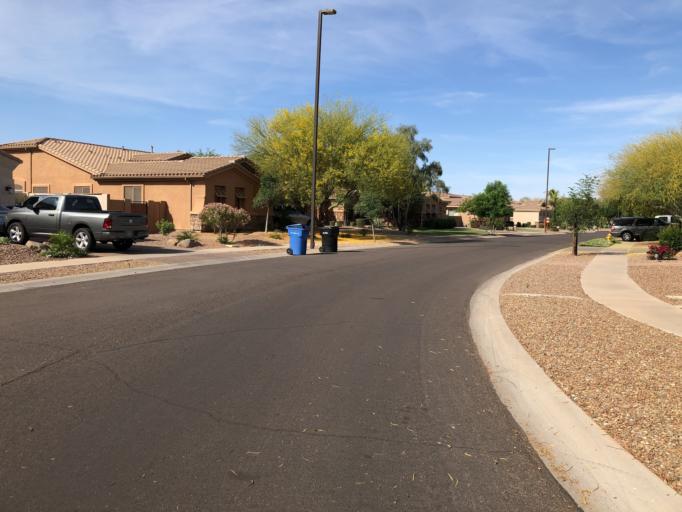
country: US
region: Arizona
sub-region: Maricopa County
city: Queen Creek
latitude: 33.2722
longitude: -111.6913
